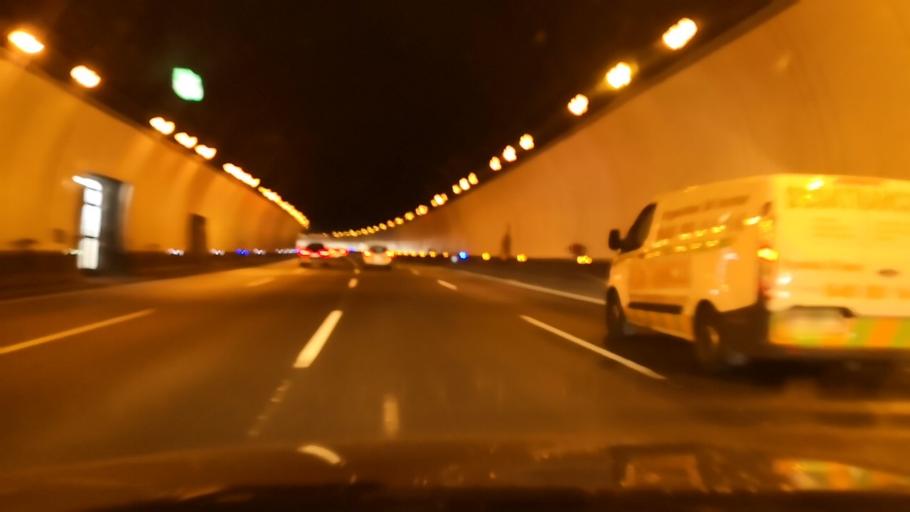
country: ES
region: Madrid
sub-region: Provincia de Madrid
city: Fuencarral-El Pardo
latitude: 40.4823
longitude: -3.7456
